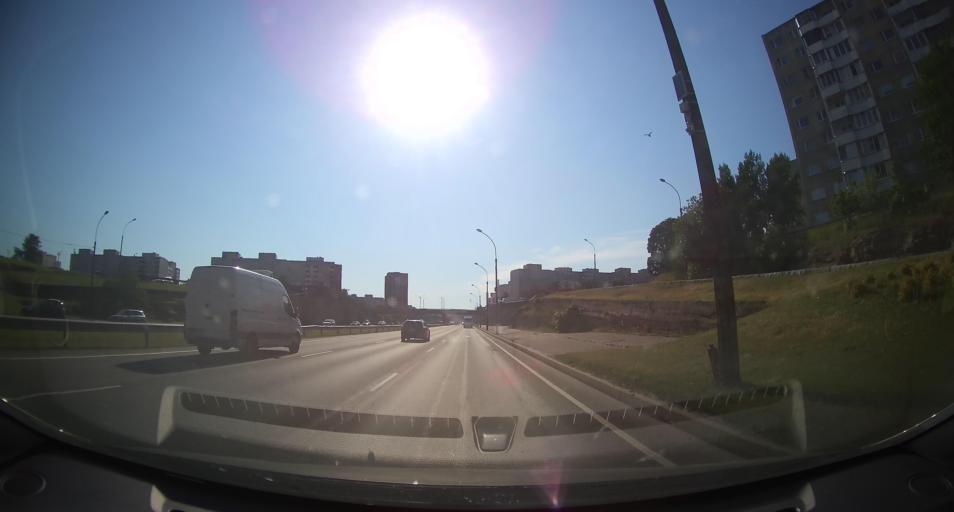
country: EE
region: Harju
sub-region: Tallinna linn
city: Kose
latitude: 59.4405
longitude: 24.8421
